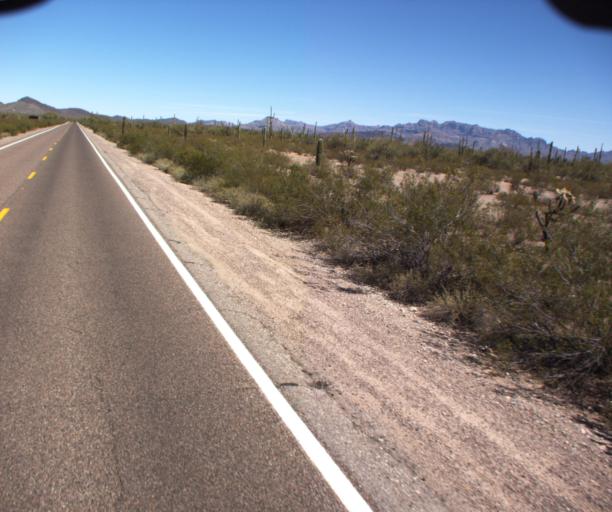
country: MX
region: Sonora
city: Sonoyta
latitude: 31.8986
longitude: -112.8116
